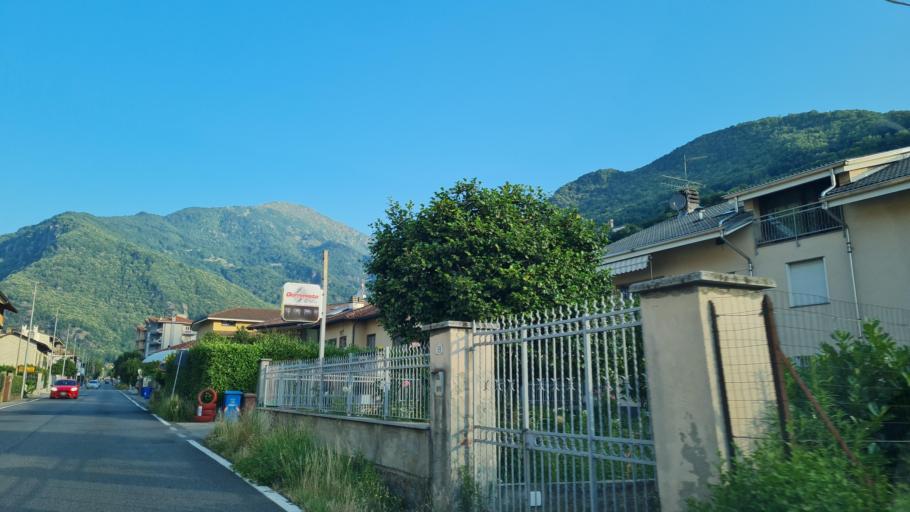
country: IT
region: Piedmont
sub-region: Provincia di Torino
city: Pont-Canavese
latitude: 45.4189
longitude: 7.6111
